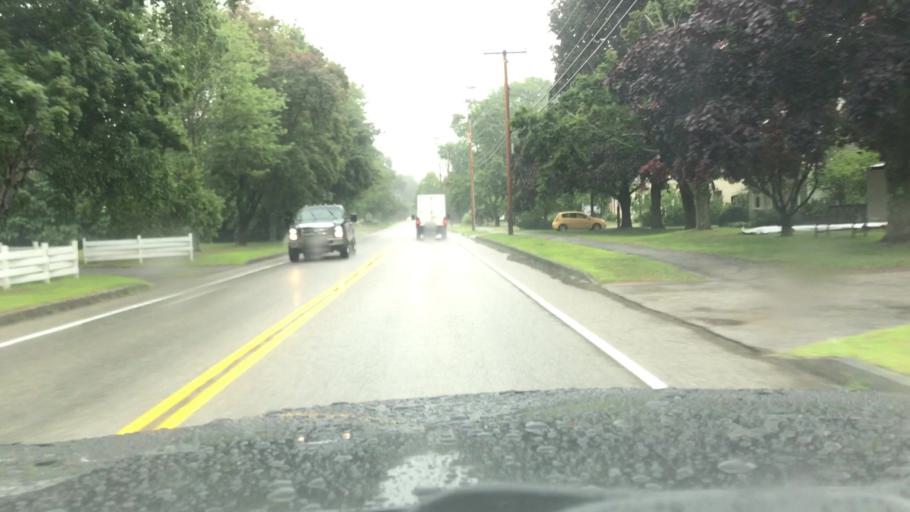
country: US
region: Maine
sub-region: York County
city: Kennebunk
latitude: 43.3942
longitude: -70.5487
